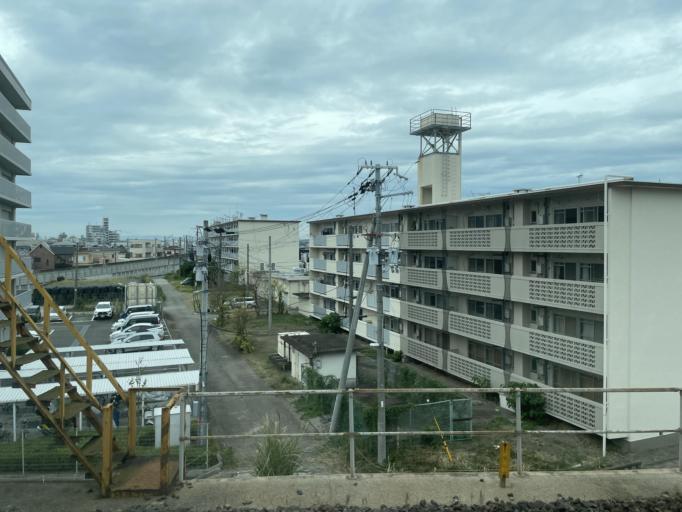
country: JP
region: Wakayama
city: Wakayama-shi
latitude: 34.2419
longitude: 135.1895
